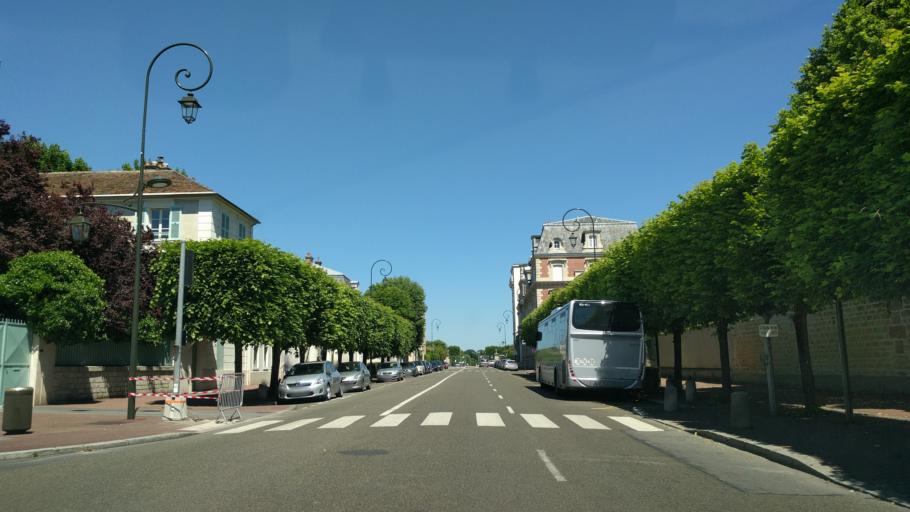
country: FR
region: Ile-de-France
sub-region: Departement des Yvelines
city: Le Pecq
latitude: 48.8963
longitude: 2.0985
